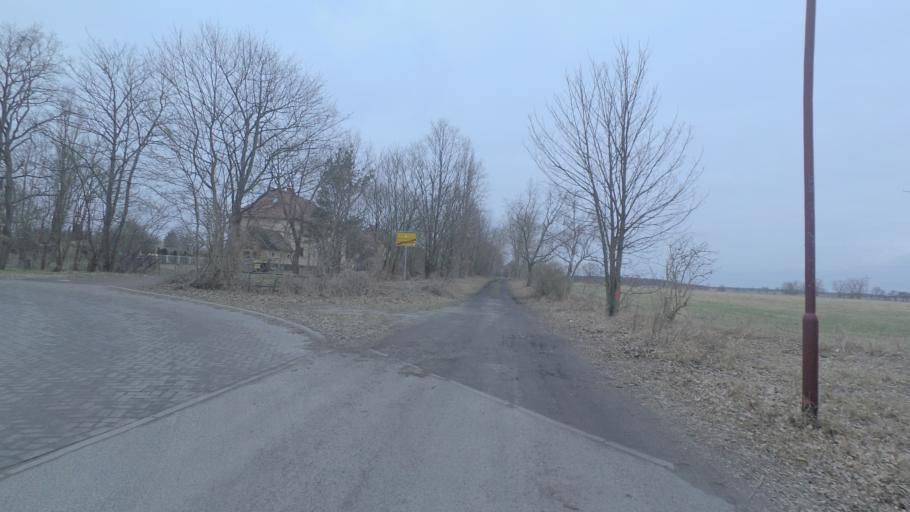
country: DE
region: Brandenburg
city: Ludwigsfelde
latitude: 52.3225
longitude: 13.2314
